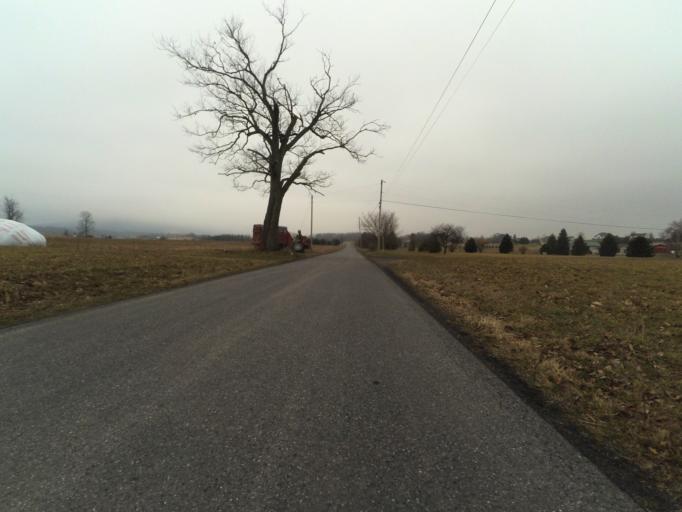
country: US
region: Pennsylvania
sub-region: Centre County
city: Centre Hall
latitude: 40.8031
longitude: -77.6749
